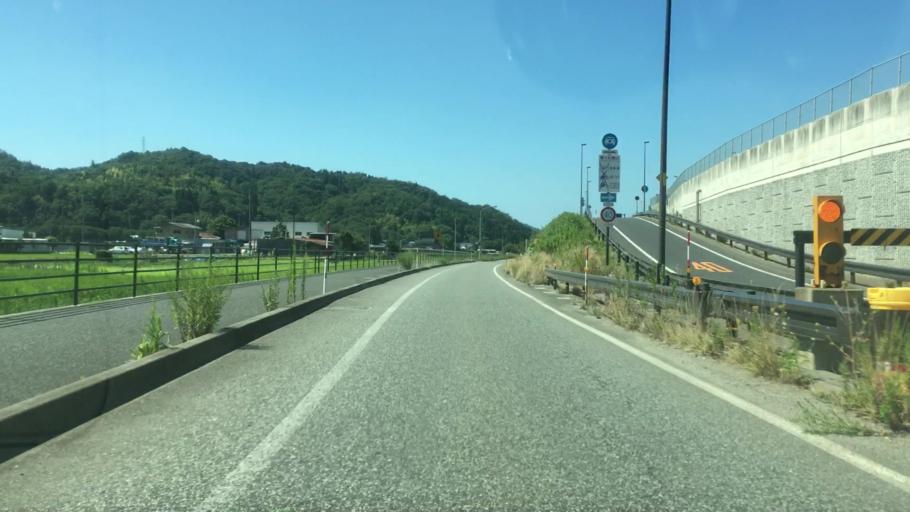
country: JP
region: Tottori
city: Tottori
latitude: 35.4310
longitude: 134.2056
